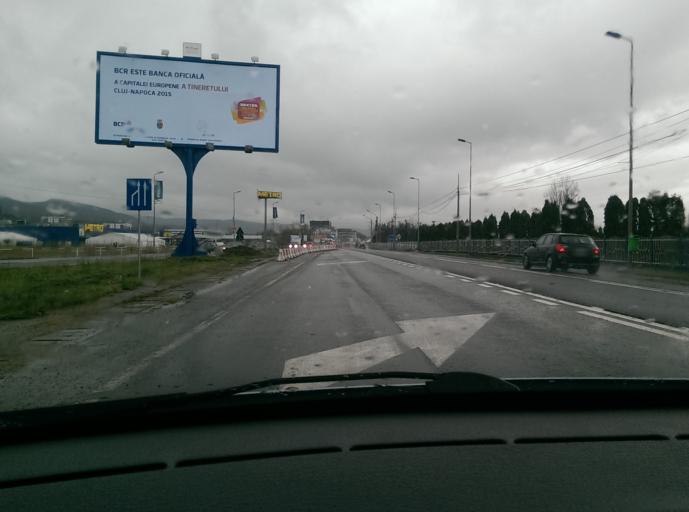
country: RO
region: Cluj
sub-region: Comuna Floresti
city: Floresti
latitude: 46.7538
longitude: 23.5300
